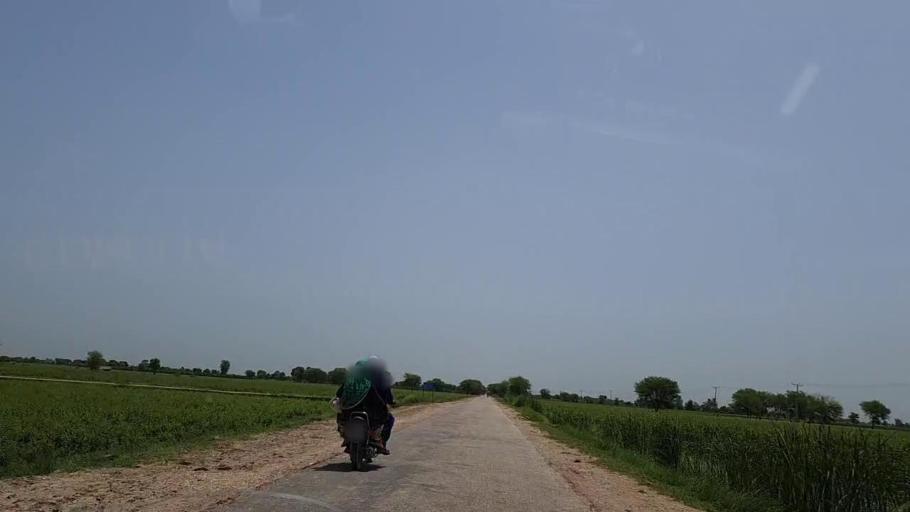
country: PK
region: Sindh
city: Tharu Shah
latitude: 26.9610
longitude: 68.0620
